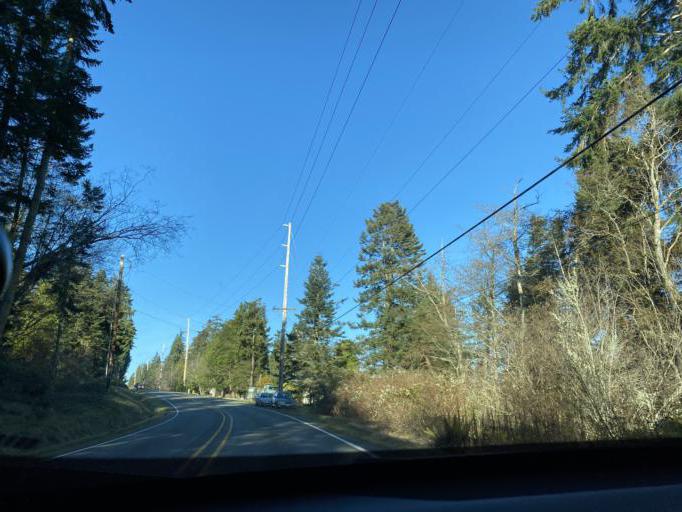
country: US
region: Washington
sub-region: Island County
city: Camano
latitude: 48.1194
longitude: -122.5613
